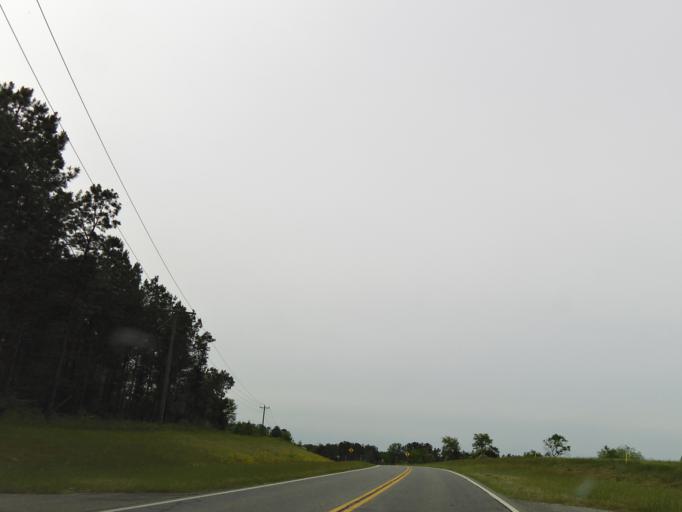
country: US
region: Georgia
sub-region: Bleckley County
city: Cochran
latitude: 32.3946
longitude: -83.3263
